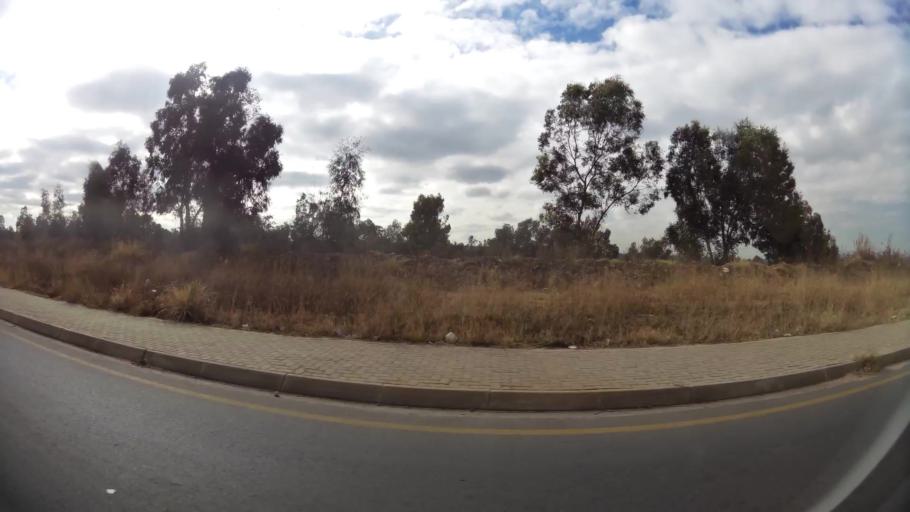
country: ZA
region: Gauteng
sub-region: City of Johannesburg Metropolitan Municipality
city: Roodepoort
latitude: -26.1972
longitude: 27.9025
